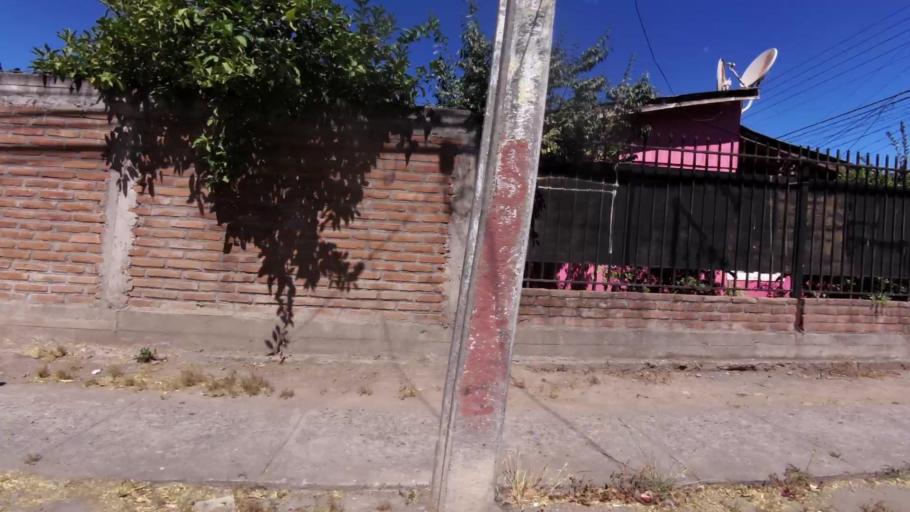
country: CL
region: O'Higgins
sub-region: Provincia de Colchagua
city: Chimbarongo
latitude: -34.5823
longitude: -70.9924
